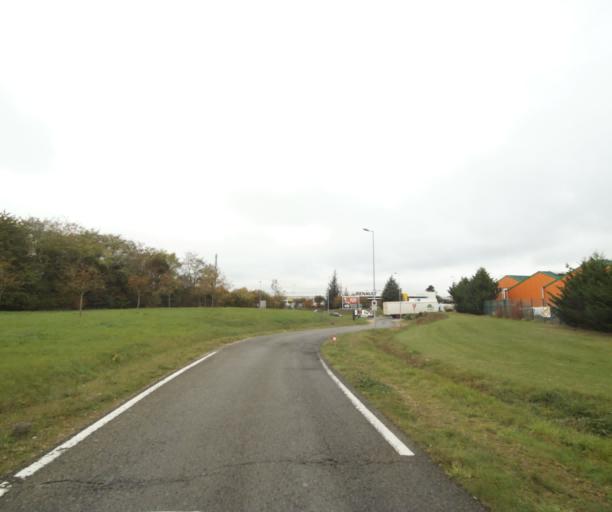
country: FR
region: Centre
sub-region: Departement d'Eure-et-Loir
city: Dreux
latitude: 48.7458
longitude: 1.3476
